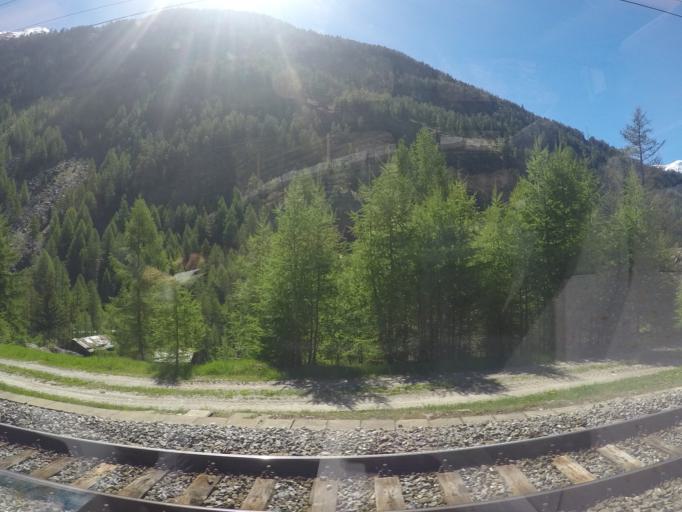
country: CH
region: Valais
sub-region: Visp District
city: Zermatt
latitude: 46.0446
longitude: 7.7657
